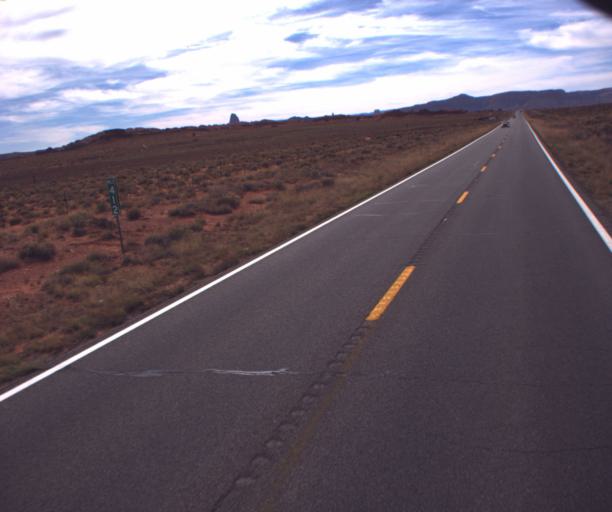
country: US
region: Arizona
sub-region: Navajo County
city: Kayenta
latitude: 36.9377
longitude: -110.2162
